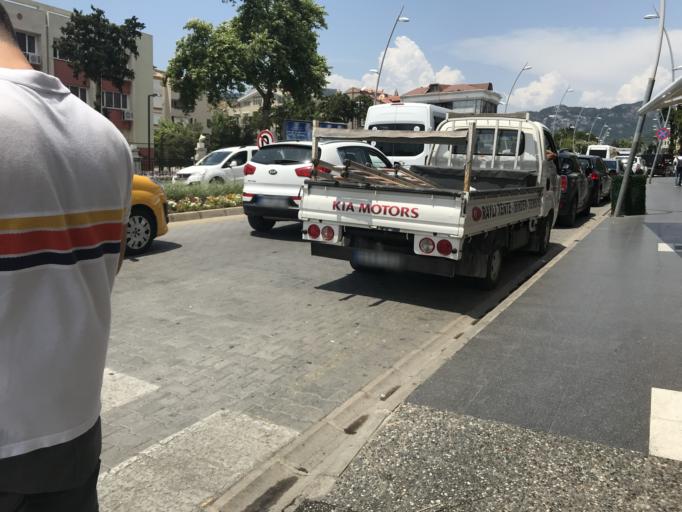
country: TR
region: Mugla
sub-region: Marmaris
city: Marmaris
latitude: 36.8535
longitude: 28.2711
